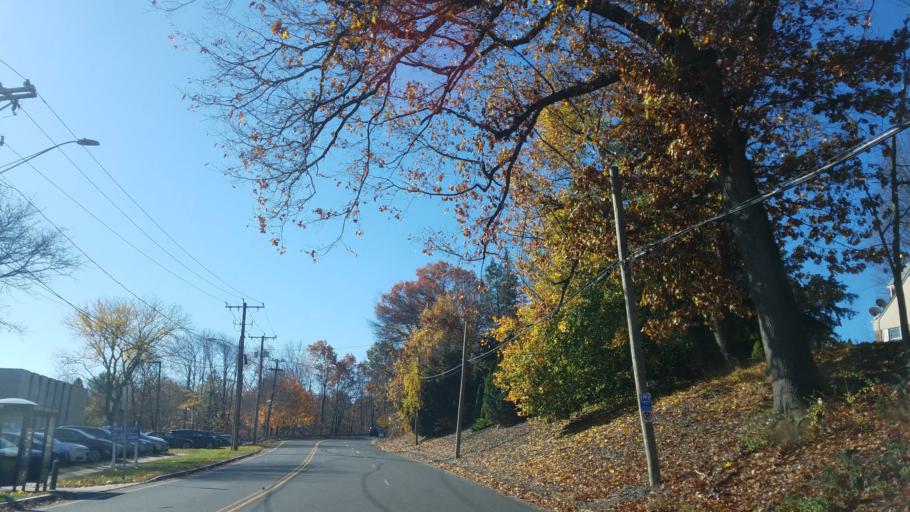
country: US
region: Connecticut
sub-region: New Haven County
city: Waterbury
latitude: 41.5499
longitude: -73.0661
